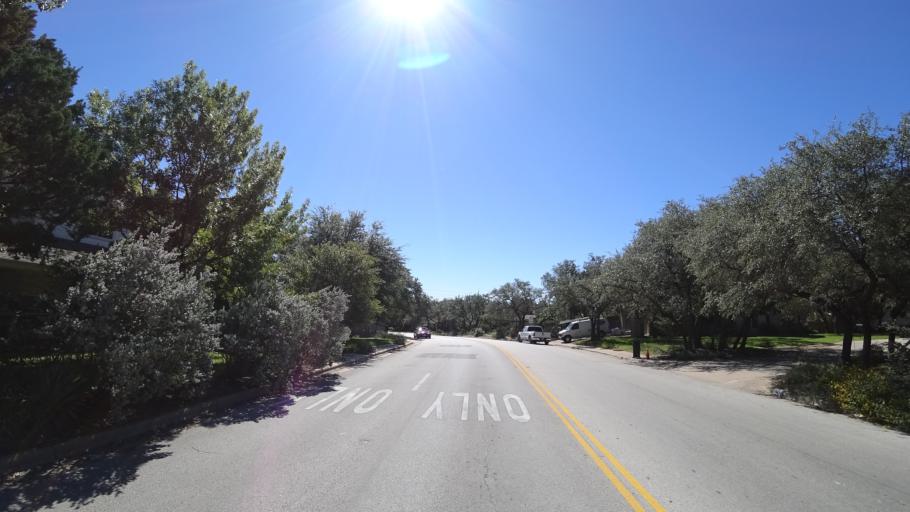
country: US
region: Texas
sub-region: Travis County
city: West Lake Hills
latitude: 30.3409
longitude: -97.7789
